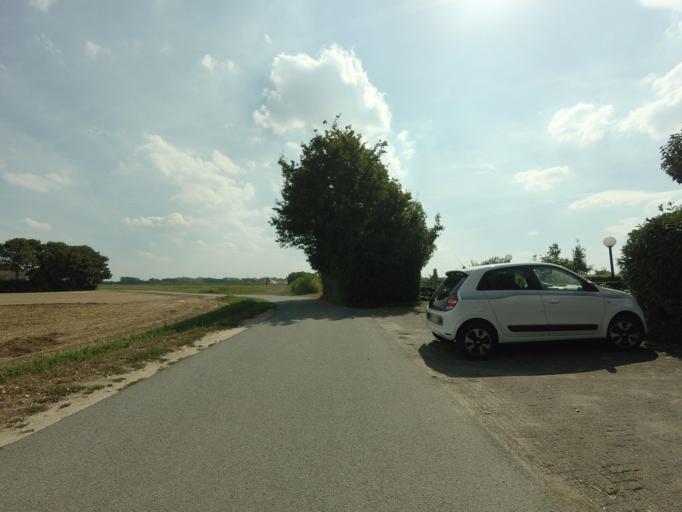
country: NL
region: Gelderland
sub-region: Gemeente Rheden
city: De Steeg
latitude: 52.0055
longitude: 6.0807
